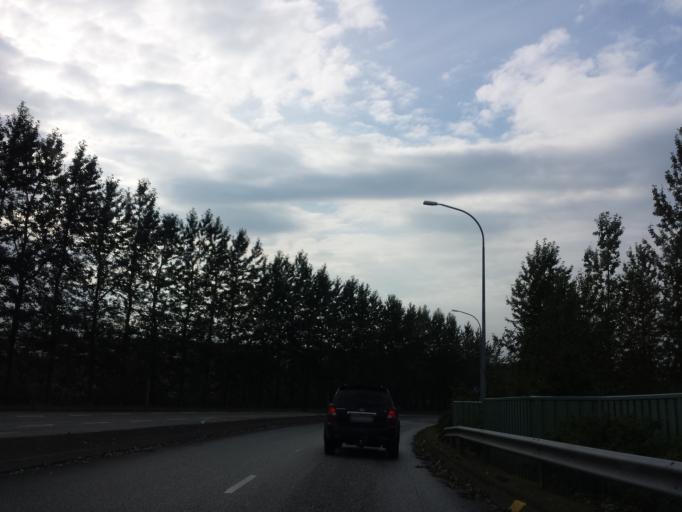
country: IS
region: Capital Region
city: Reykjavik
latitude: 64.1073
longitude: -21.8534
